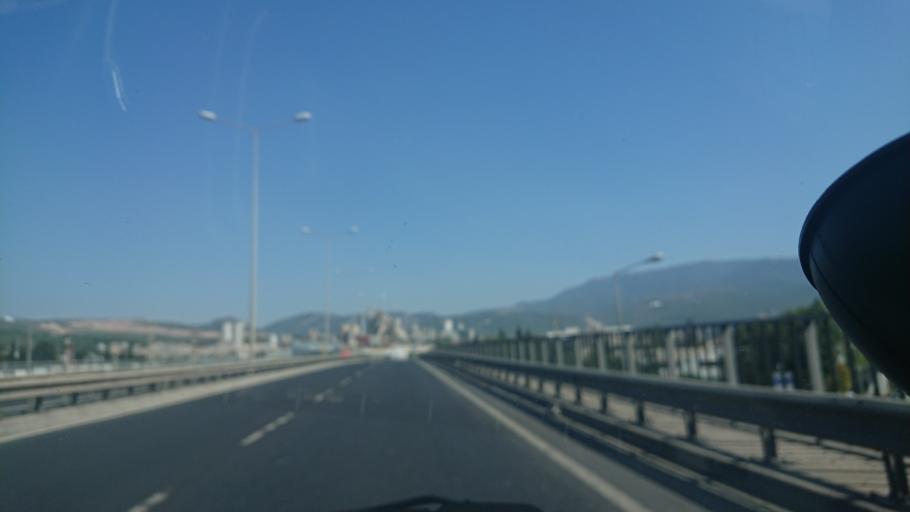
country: TR
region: Izmir
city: Bornova
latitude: 38.4577
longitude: 27.2502
